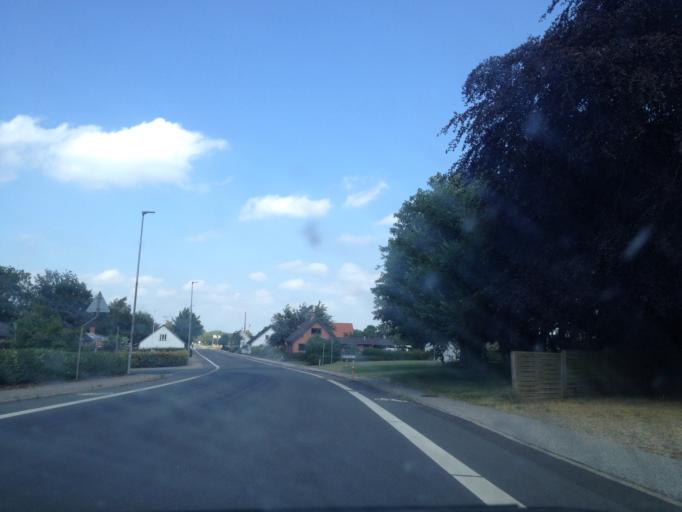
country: DK
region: South Denmark
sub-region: Kolding Kommune
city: Vamdrup
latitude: 55.4181
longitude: 9.2708
